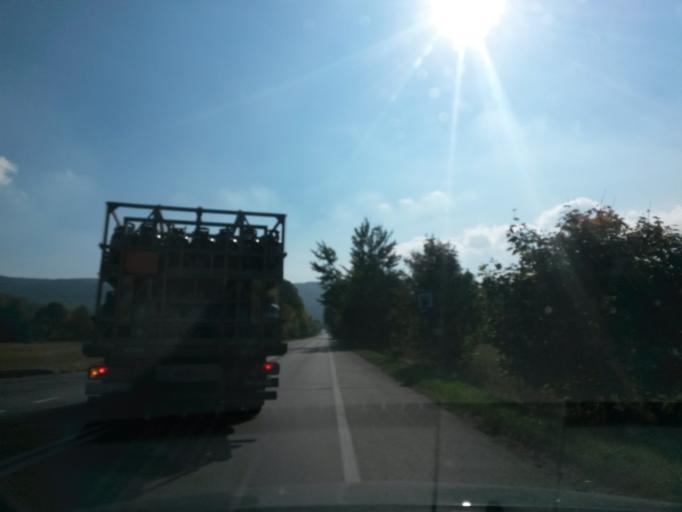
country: PL
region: Lower Silesian Voivodeship
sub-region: Powiat jeleniogorski
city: Kowary
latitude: 50.7997
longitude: 15.8410
